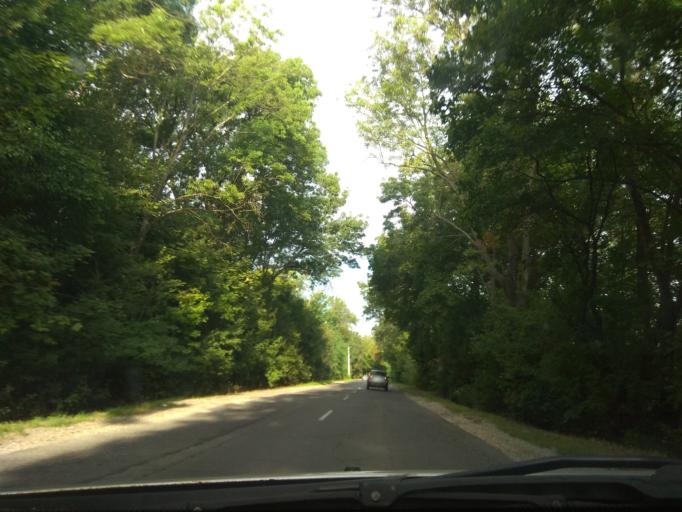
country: HU
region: Borsod-Abauj-Zemplen
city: Miskolc
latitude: 48.0878
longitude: 20.7355
